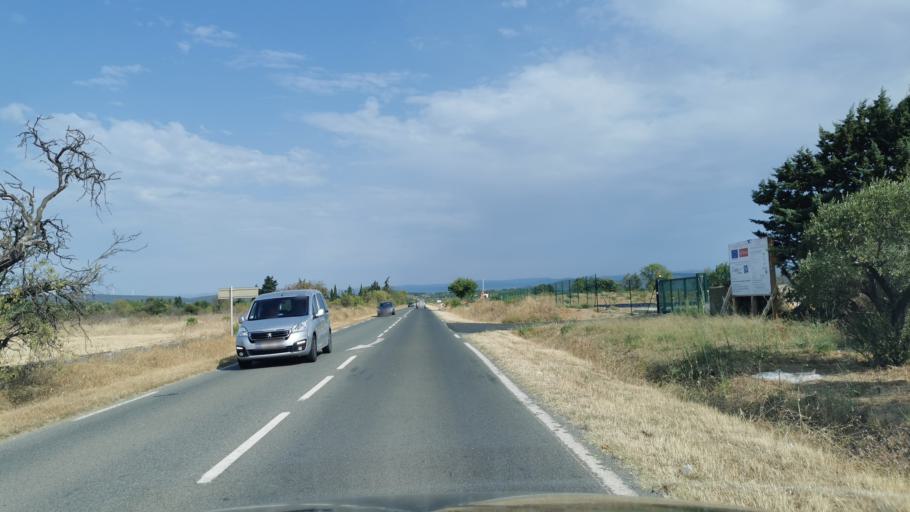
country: FR
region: Languedoc-Roussillon
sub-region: Departement de l'Aude
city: Ginestas
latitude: 43.2766
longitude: 2.8848
